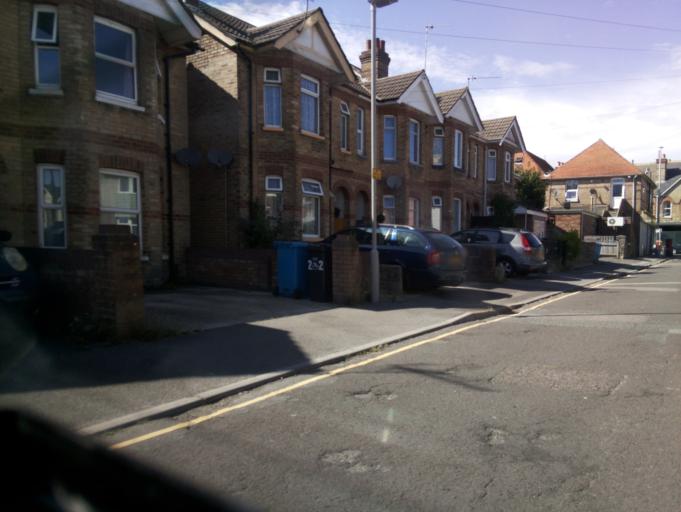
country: GB
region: England
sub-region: Dorset
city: Parkstone
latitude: 50.7285
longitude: -1.9434
